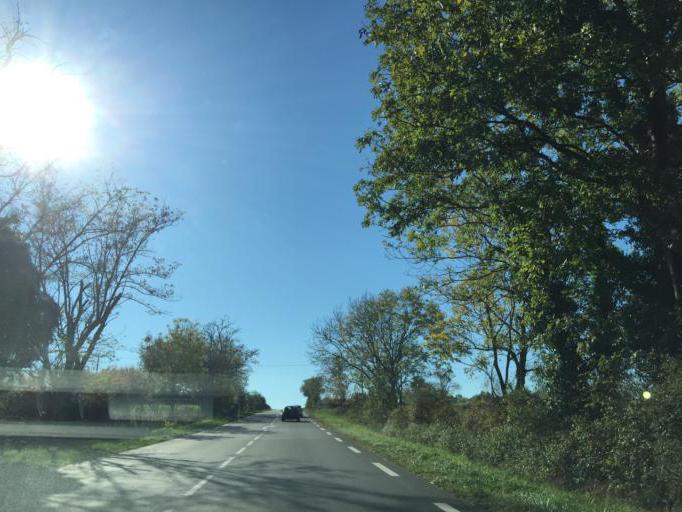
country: FR
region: Rhone-Alpes
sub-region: Departement du Rhone
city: Saint-Andeol-le-Chateau
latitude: 45.5974
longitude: 4.6785
